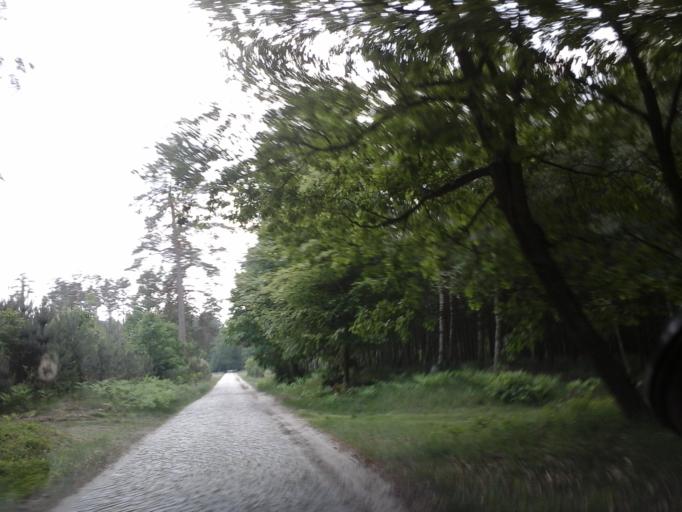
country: PL
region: West Pomeranian Voivodeship
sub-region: Powiat choszczenski
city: Drawno
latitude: 53.1185
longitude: 15.8059
